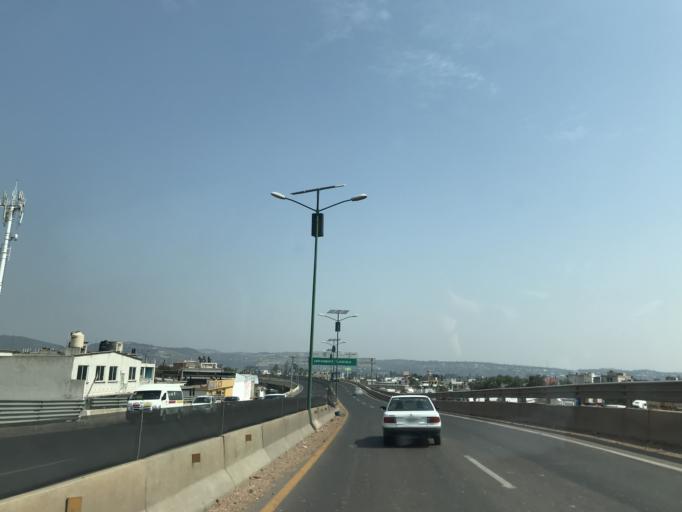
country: MX
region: Tlaxcala
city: Tlaxcala de Xicohtencatl
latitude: 19.3085
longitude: -98.2000
